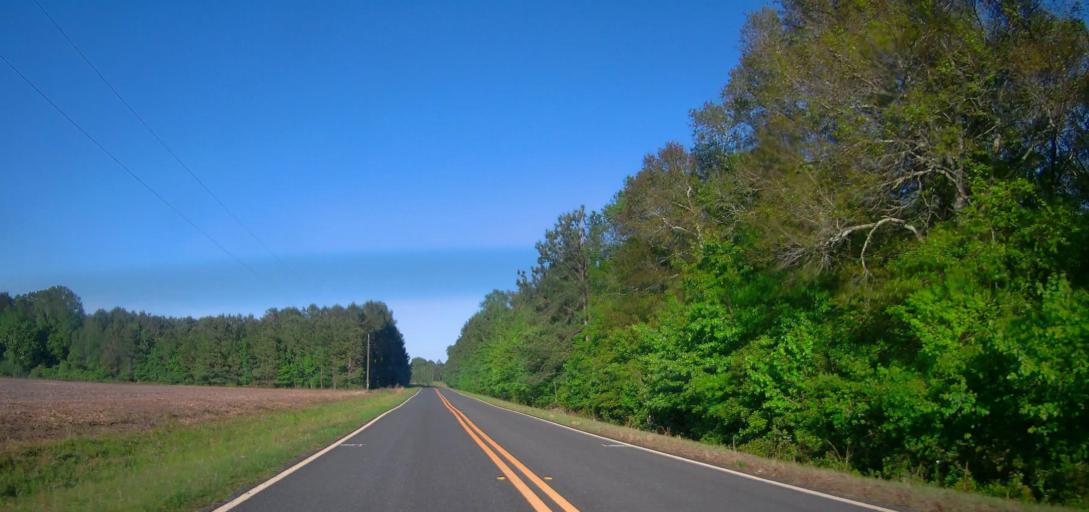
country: US
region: Georgia
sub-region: Macon County
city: Marshallville
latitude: 32.3847
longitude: -83.8598
